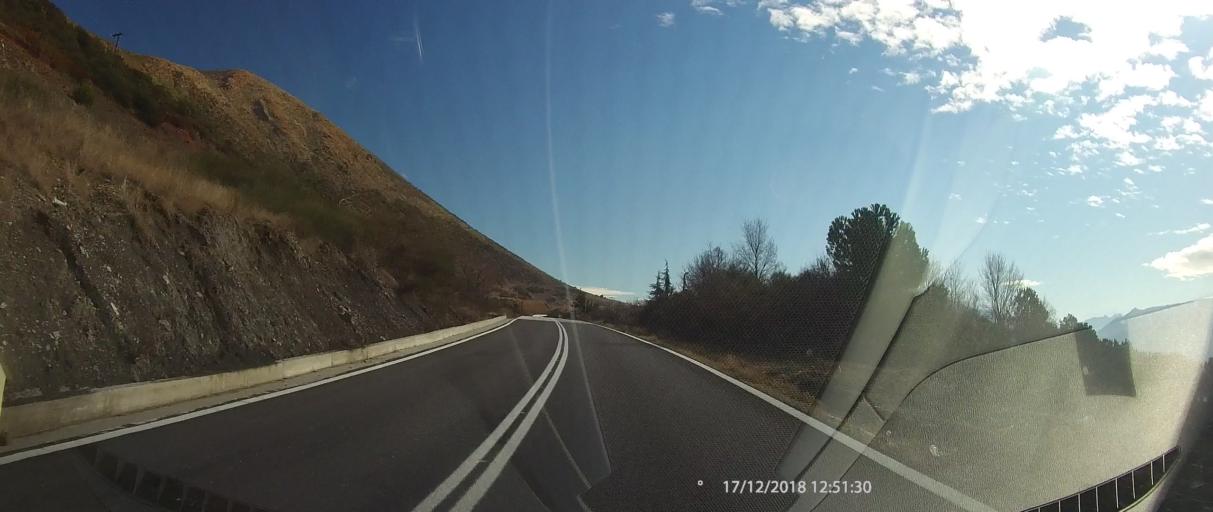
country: GR
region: Thessaly
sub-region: Trikala
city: Kastraki
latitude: 39.7656
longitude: 21.4656
